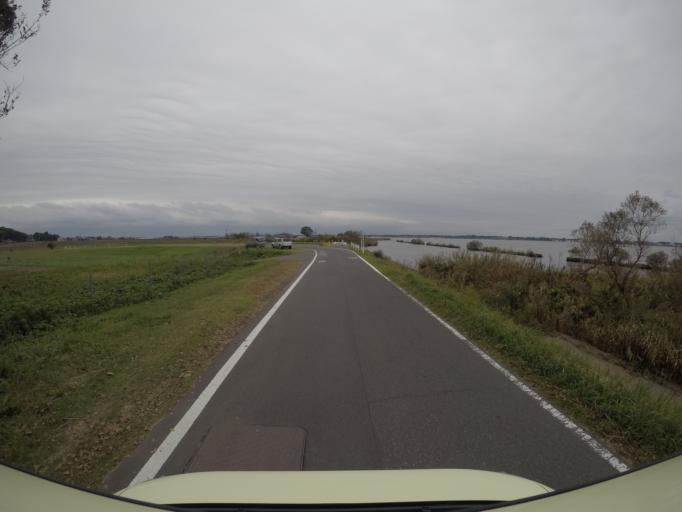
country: JP
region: Ibaraki
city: Ami
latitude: 36.0753
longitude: 140.2399
